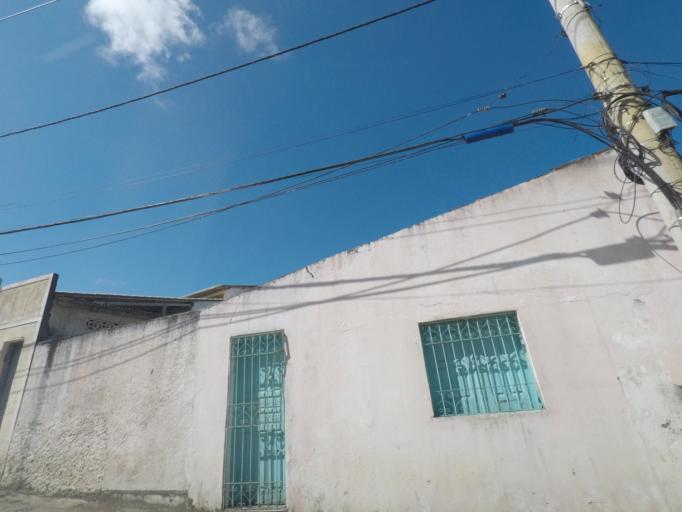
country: BR
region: Bahia
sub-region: Camamu
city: Camamu
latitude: -13.9459
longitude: -39.1041
